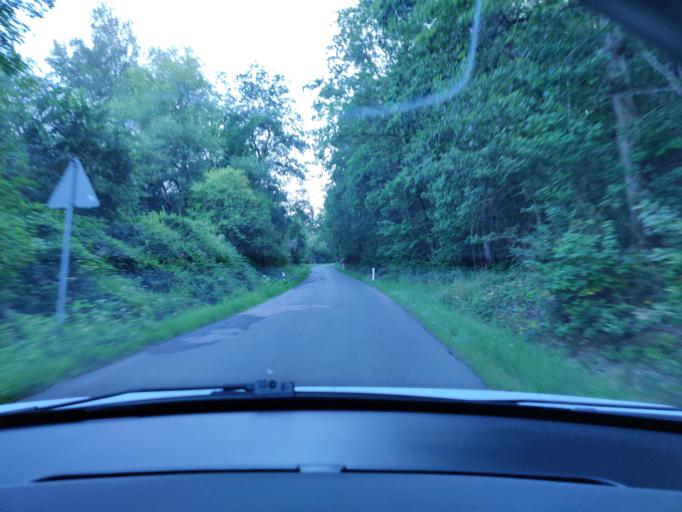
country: DE
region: Bavaria
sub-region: Upper Palatinate
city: Nabburg
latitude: 49.4292
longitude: 12.1670
